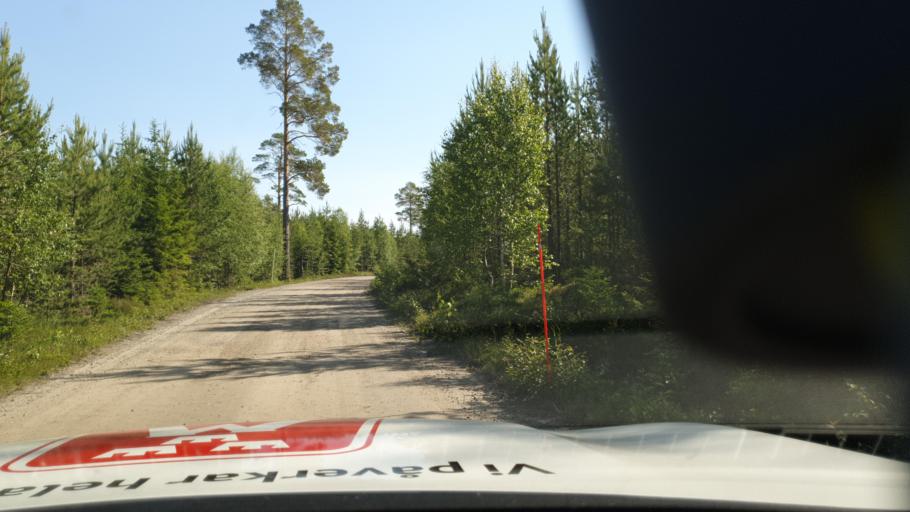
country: SE
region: Vaesterbotten
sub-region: Robertsfors Kommun
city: Robertsfors
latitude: 64.2273
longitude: 21.0440
